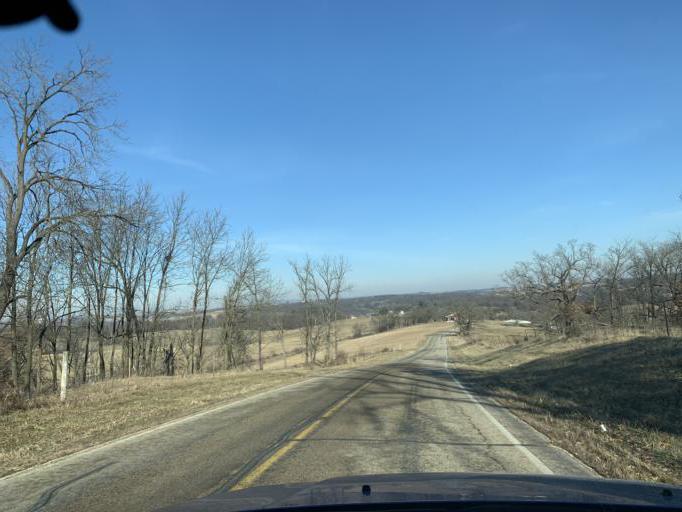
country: US
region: Wisconsin
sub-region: Iowa County
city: Barneveld
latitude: 42.8629
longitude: -89.9394
